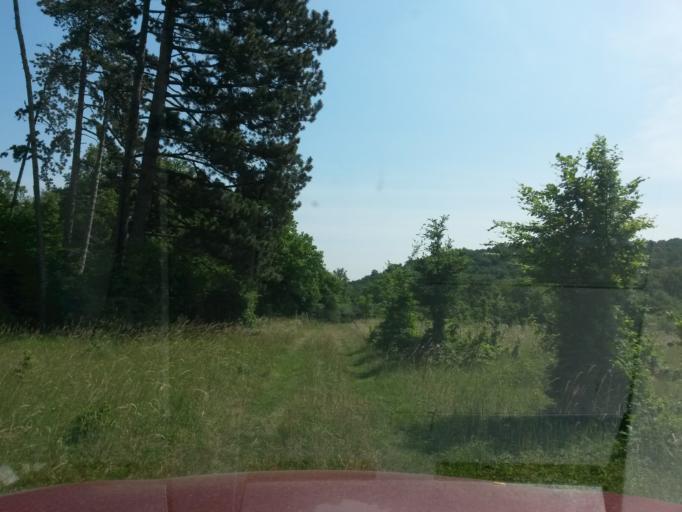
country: SK
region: Kosicky
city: Moldava nad Bodvou
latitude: 48.6453
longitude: 20.9525
